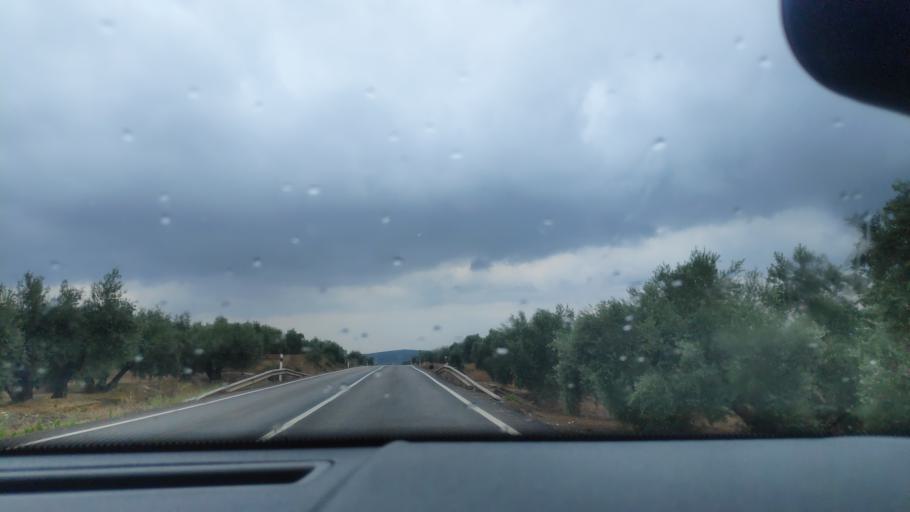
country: ES
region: Andalusia
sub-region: Provincia de Jaen
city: Jabalquinto
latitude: 38.0389
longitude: -3.7430
